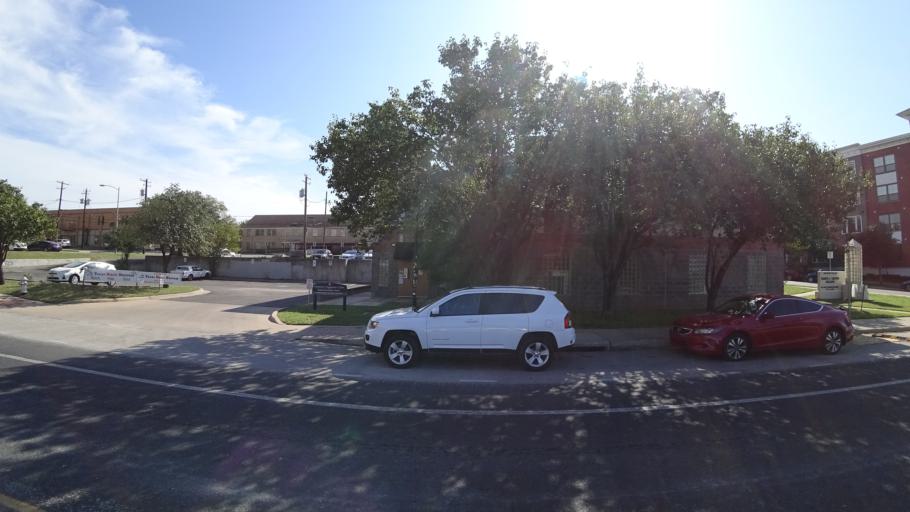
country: US
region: Texas
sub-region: Travis County
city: Austin
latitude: 30.2697
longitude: -97.7304
